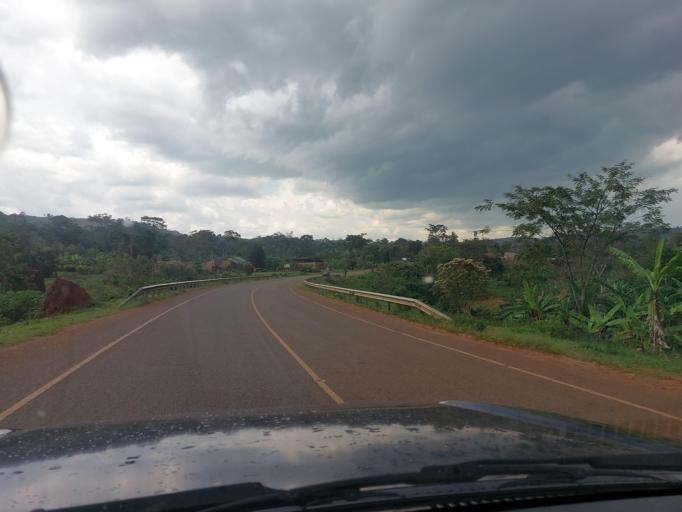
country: UG
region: Central Region
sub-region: Mukono District
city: Mukono
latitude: 0.2644
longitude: 32.8382
